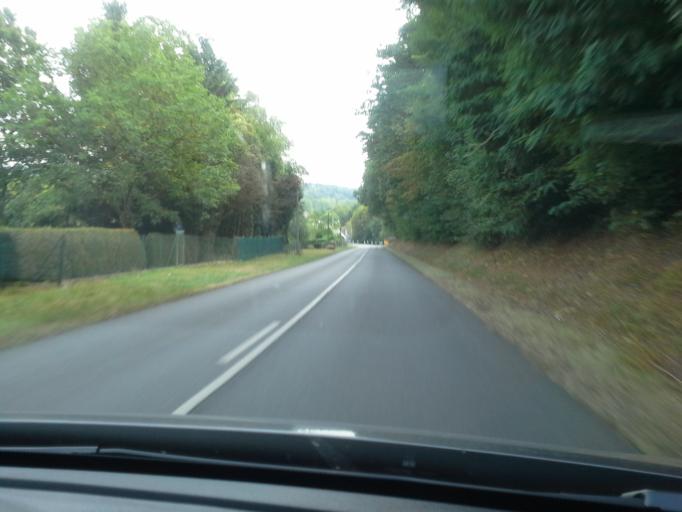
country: FR
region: Centre
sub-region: Departement du Loir-et-Cher
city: Saint-Sulpice-de-Pommeray
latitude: 47.5808
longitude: 1.2088
